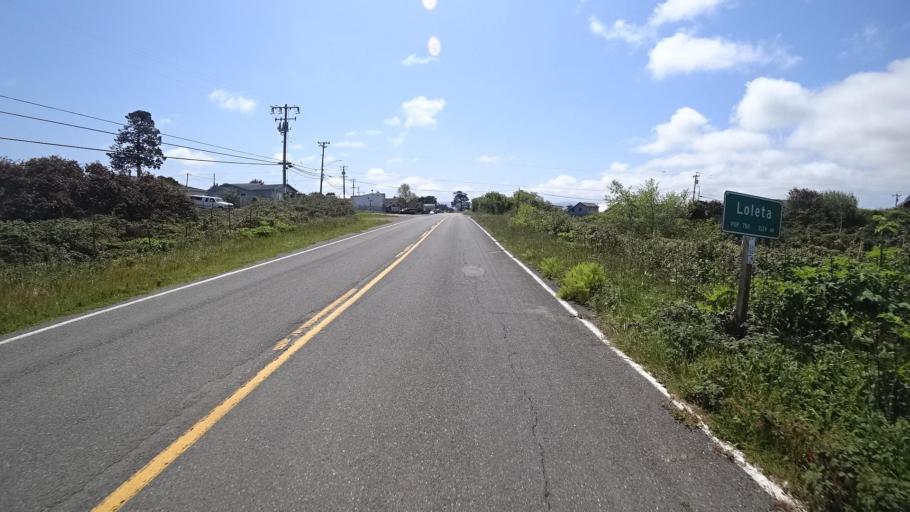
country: US
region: California
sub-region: Humboldt County
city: Ferndale
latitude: 40.6433
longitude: -124.2265
